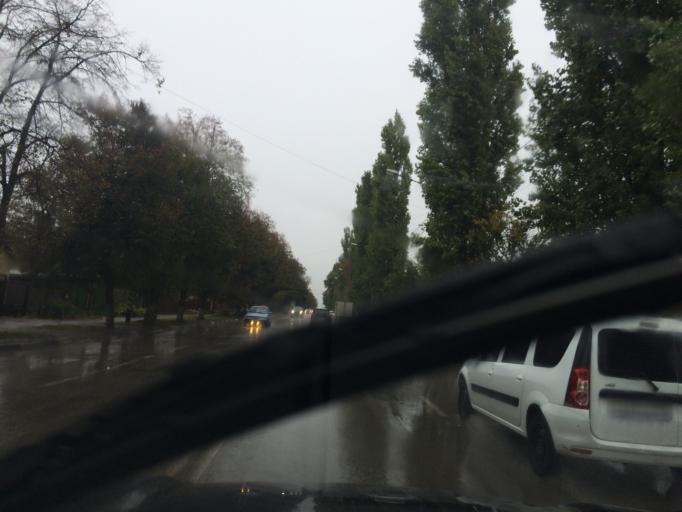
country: RU
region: Rostov
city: Azov
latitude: 47.0962
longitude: 39.4457
